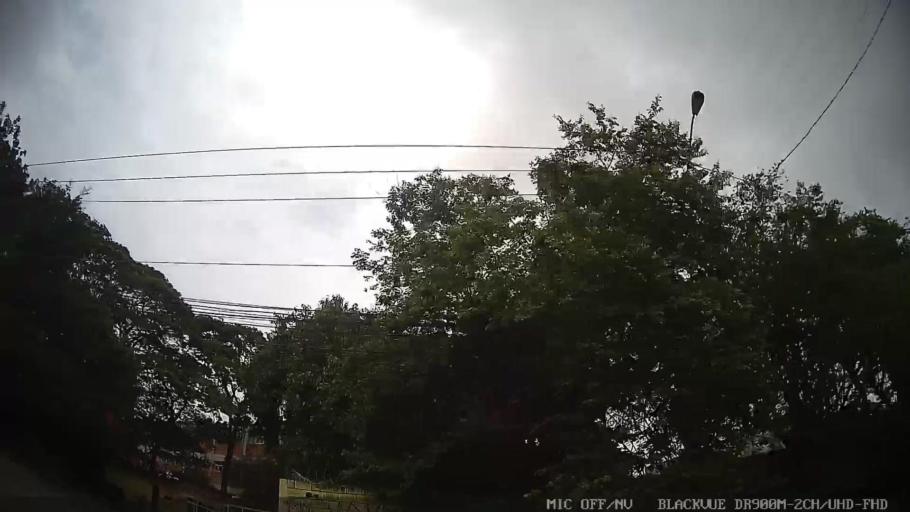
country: BR
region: Sao Paulo
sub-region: Osasco
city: Osasco
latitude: -23.4823
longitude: -46.7723
